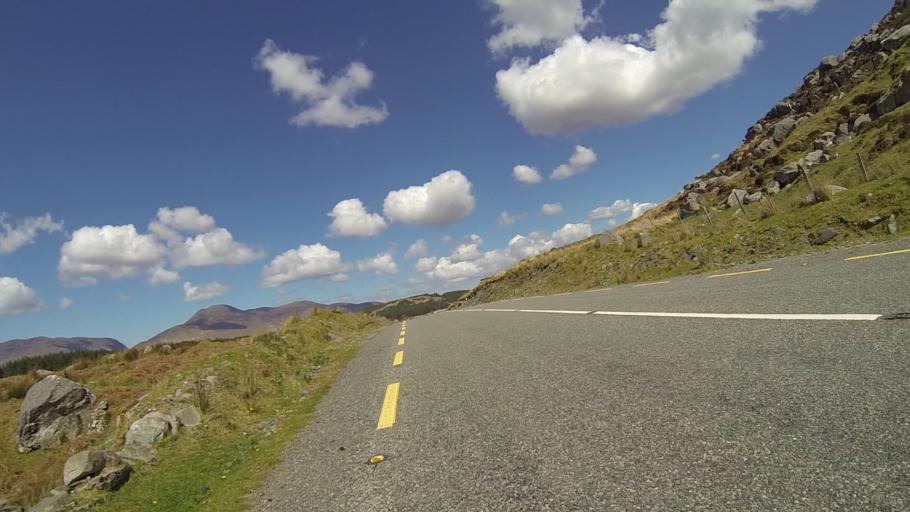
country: IE
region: Munster
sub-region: Ciarrai
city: Kenmare
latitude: 51.9497
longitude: -9.6282
